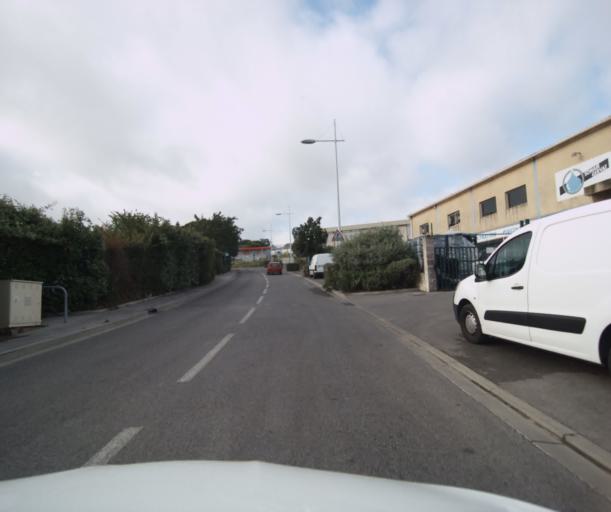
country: FR
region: Provence-Alpes-Cote d'Azur
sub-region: Departement du Var
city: Six-Fours-les-Plages
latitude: 43.1138
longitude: 5.8502
